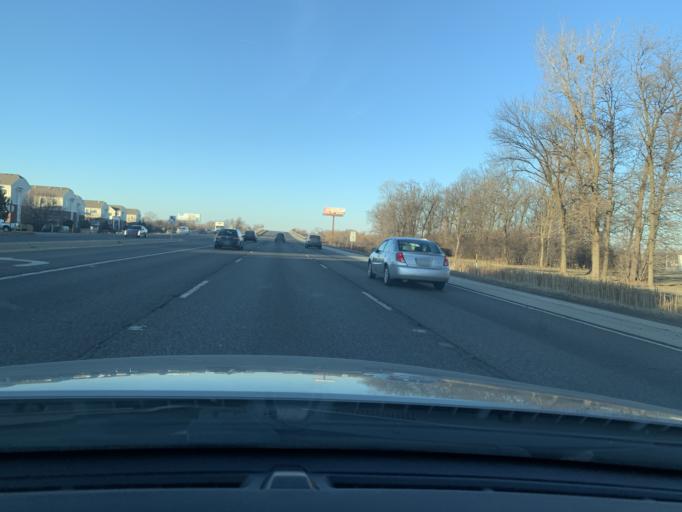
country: US
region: Illinois
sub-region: DuPage County
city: Bensenville
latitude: 41.9566
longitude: -87.9593
